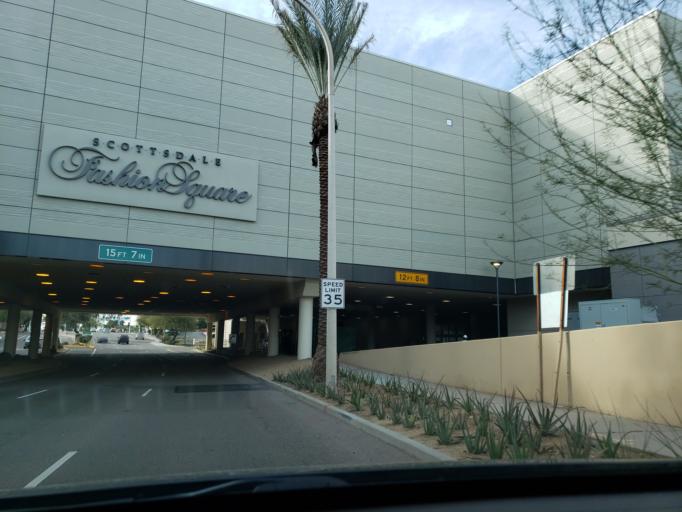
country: US
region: Arizona
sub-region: Maricopa County
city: Paradise Valley
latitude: 33.5042
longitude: -111.9307
